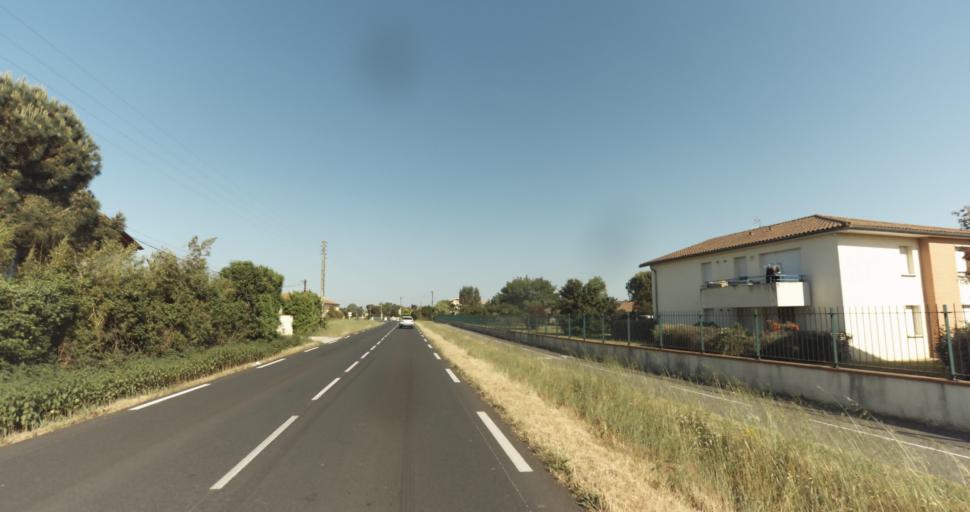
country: FR
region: Midi-Pyrenees
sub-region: Departement de la Haute-Garonne
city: Plaisance-du-Touch
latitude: 43.5526
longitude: 1.3118
